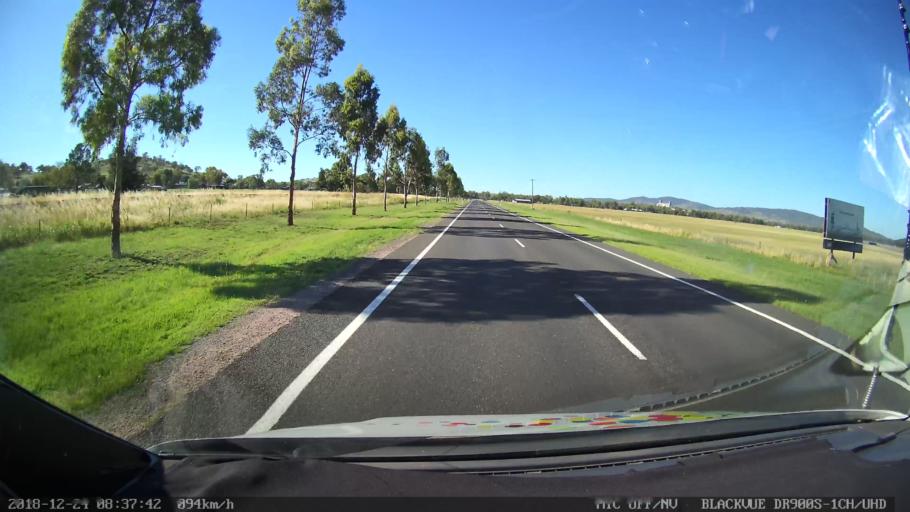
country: AU
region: New South Wales
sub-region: Liverpool Plains
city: Quirindi
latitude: -31.3325
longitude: 150.6484
